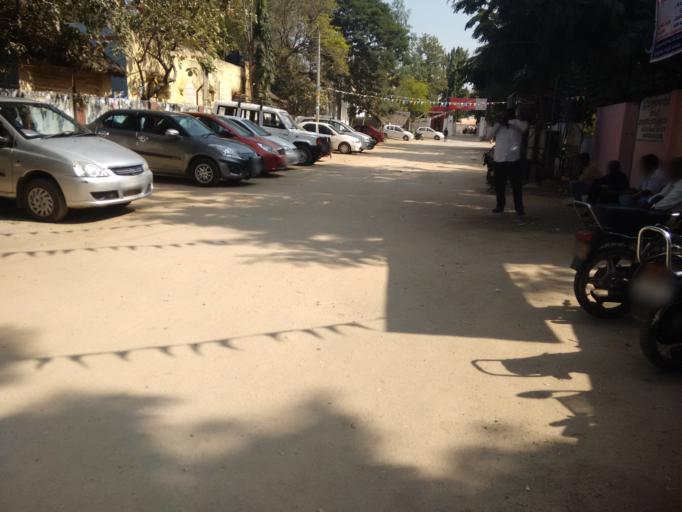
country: IN
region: Andhra Pradesh
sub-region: Chittoor
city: Chittoor
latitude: 13.2161
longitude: 79.1003
